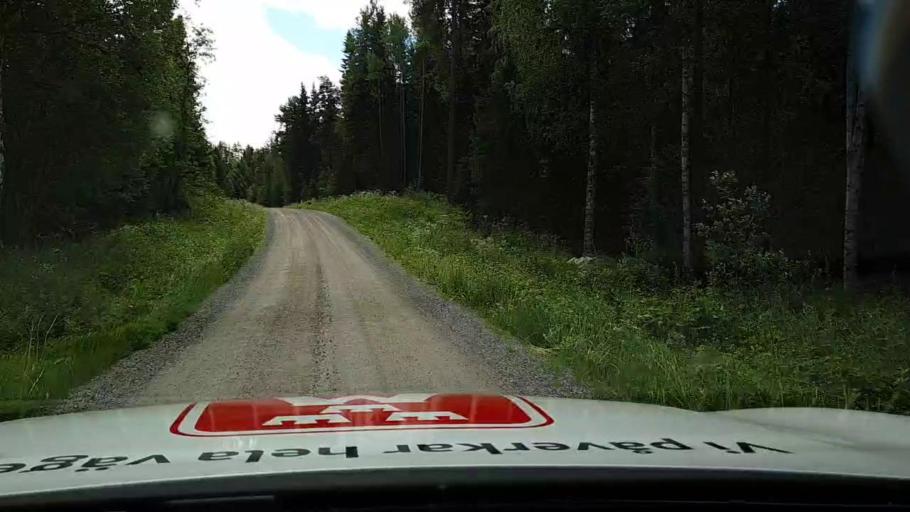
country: SE
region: Jaemtland
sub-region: Braecke Kommun
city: Braecke
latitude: 62.7582
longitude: 15.5006
